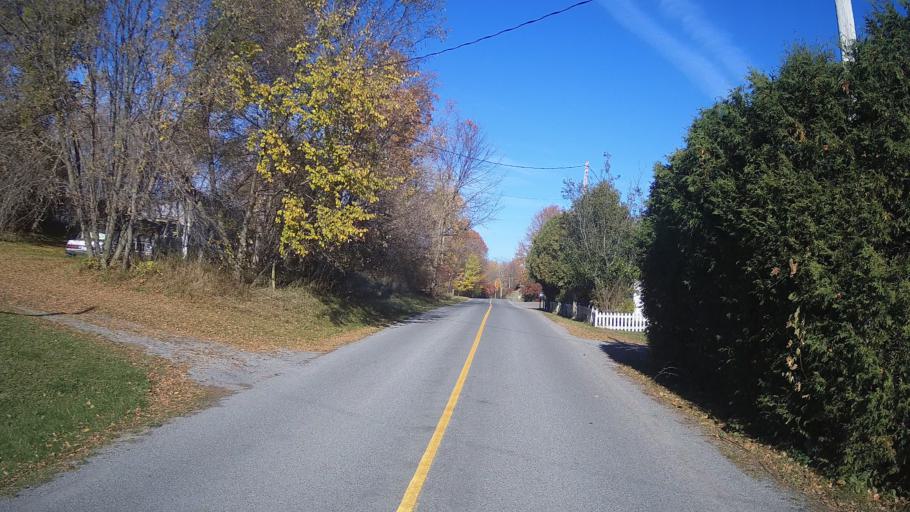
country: CA
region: Ontario
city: Kingston
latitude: 44.4497
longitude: -76.5101
